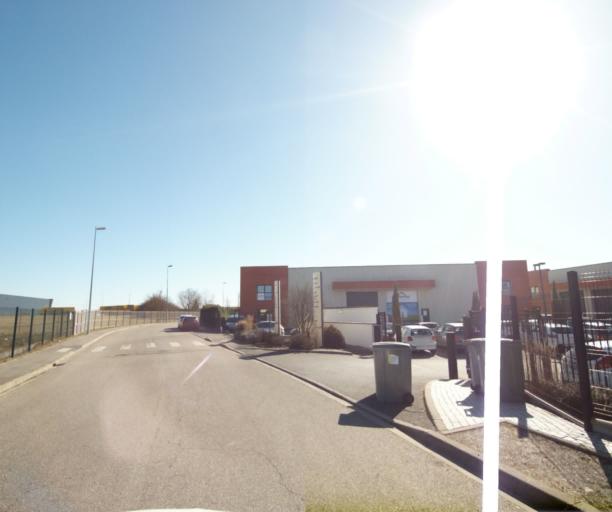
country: FR
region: Lorraine
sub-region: Departement de Meurthe-et-Moselle
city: Fleville-devant-Nancy
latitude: 48.6156
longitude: 6.2054
